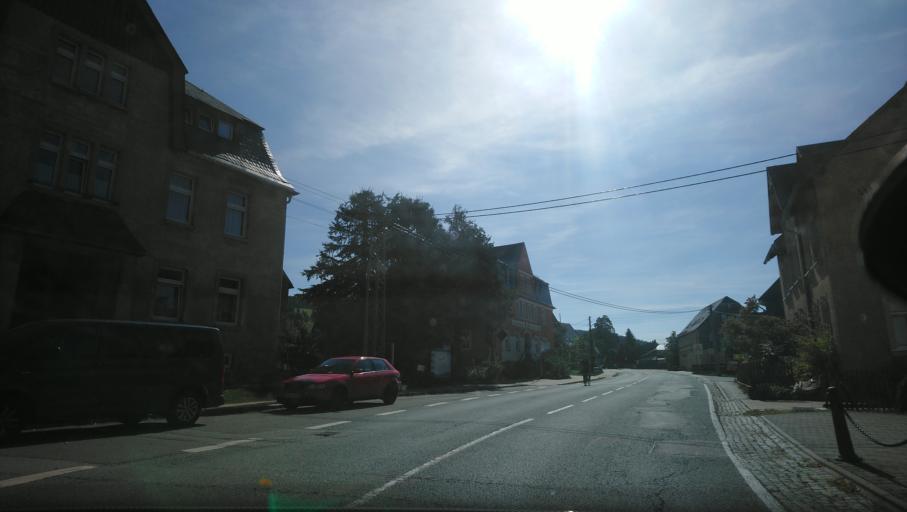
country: DE
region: Saxony
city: Konigswalde
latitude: 50.5463
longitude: 13.0490
